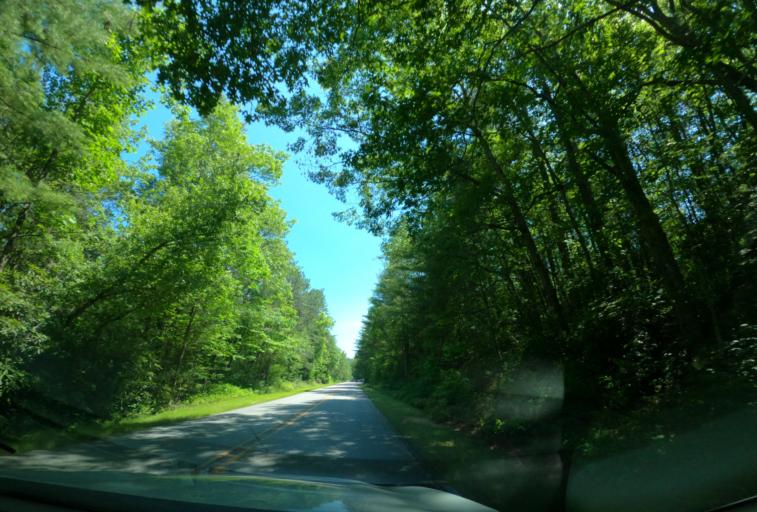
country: US
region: North Carolina
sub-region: Transylvania County
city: Brevard
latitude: 35.1742
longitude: -82.6387
